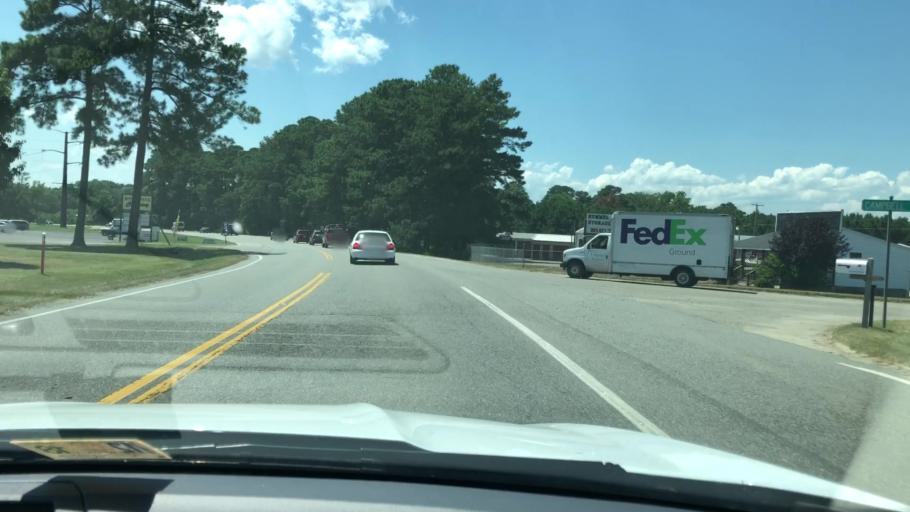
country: US
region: Virginia
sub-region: Middlesex County
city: Deltaville
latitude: 37.5985
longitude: -76.4502
